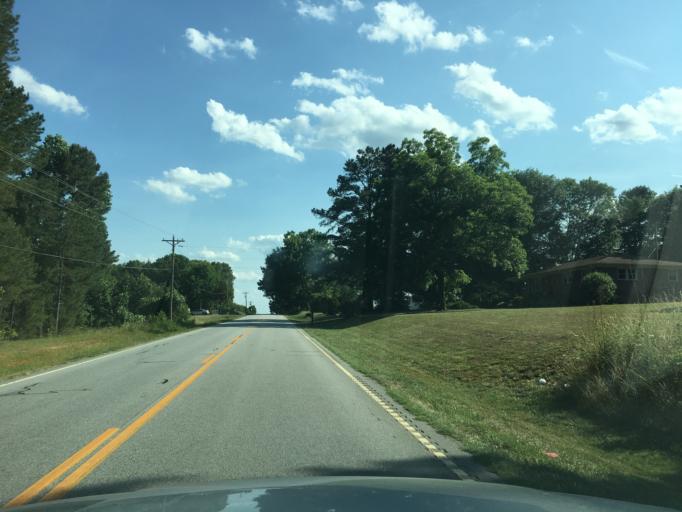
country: US
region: South Carolina
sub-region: Laurens County
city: Watts Mills
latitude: 34.5578
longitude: -81.9453
